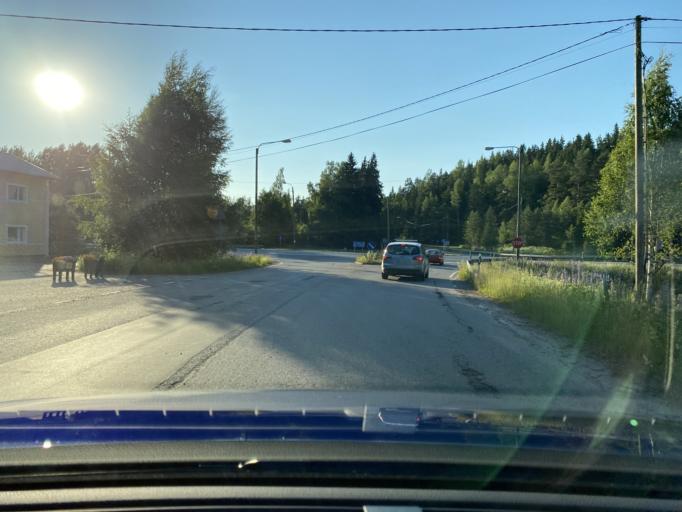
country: FI
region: Haeme
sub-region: Haemeenlinna
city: Tervakoski
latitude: 60.7440
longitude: 24.6484
